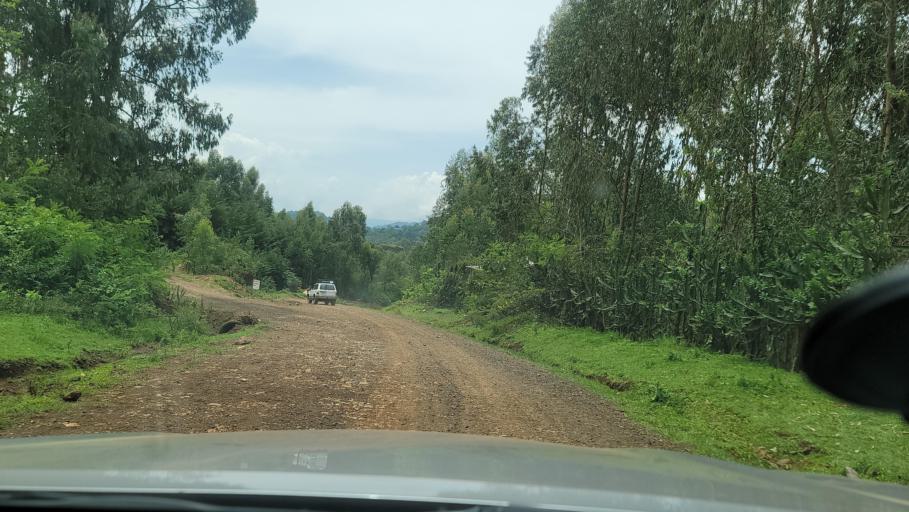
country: ET
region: Oromiya
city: Agaro
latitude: 7.7353
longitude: 36.2595
